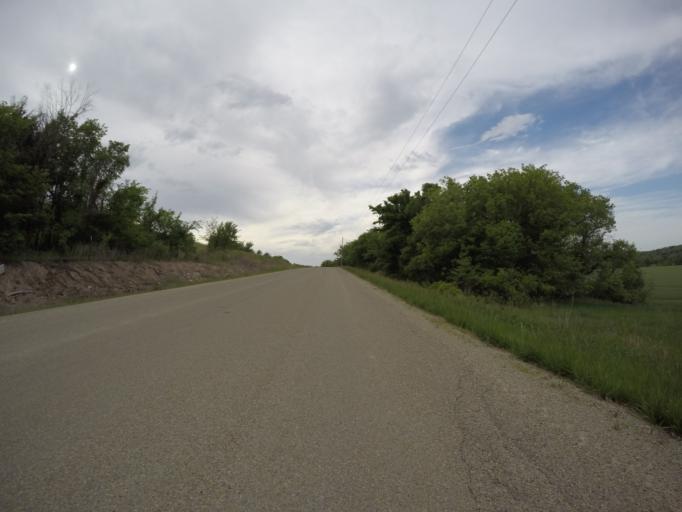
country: US
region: Kansas
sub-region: Riley County
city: Ogden
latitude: 39.0405
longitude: -96.6310
